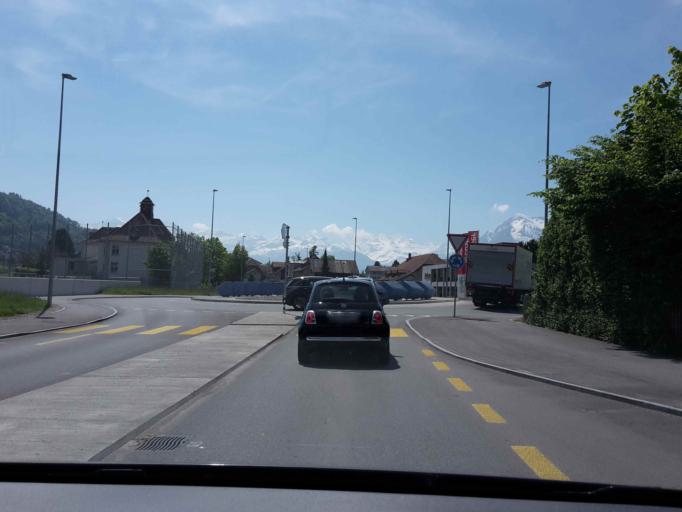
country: CH
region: Bern
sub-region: Thun District
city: Steffisburg
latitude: 46.7706
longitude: 7.6187
